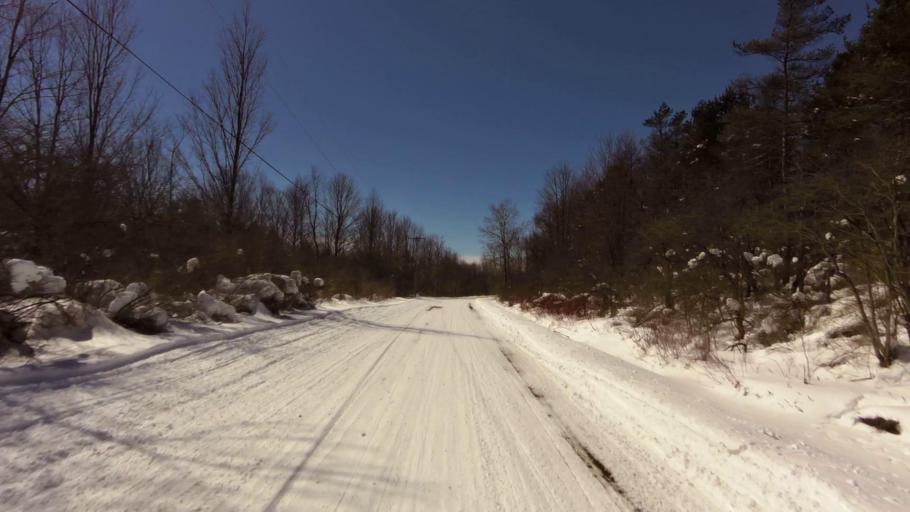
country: US
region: New York
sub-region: Wyoming County
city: Arcade
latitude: 42.4415
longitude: -78.3307
